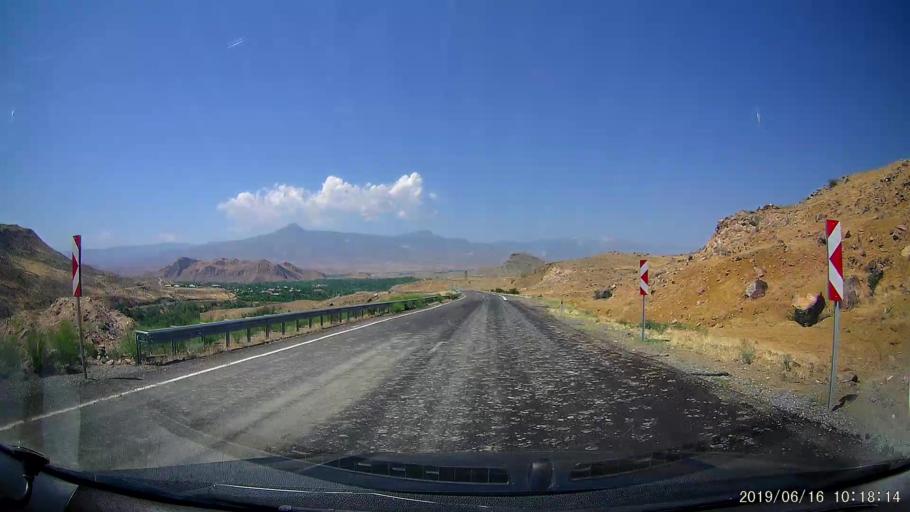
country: TR
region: Igdir
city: Tuzluca
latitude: 40.1623
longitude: 43.6707
